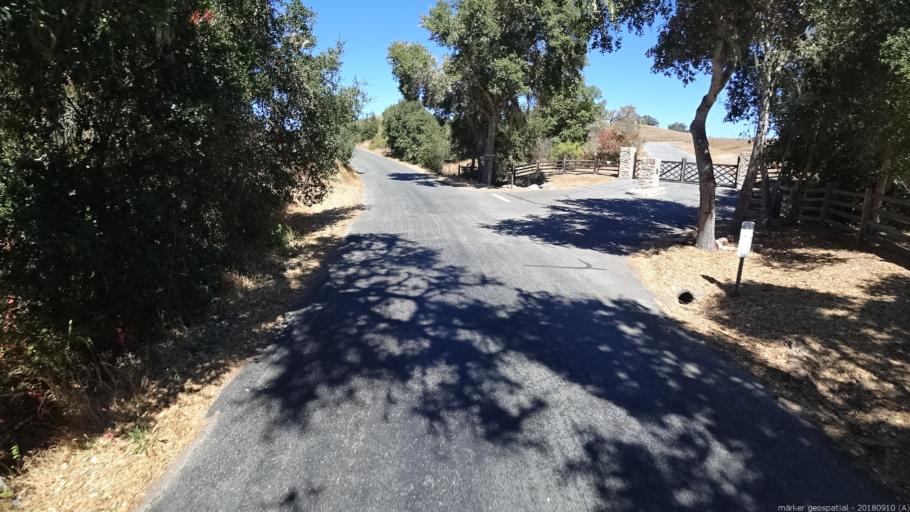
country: US
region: California
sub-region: Monterey County
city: Carmel Valley Village
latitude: 36.4653
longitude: -121.7991
